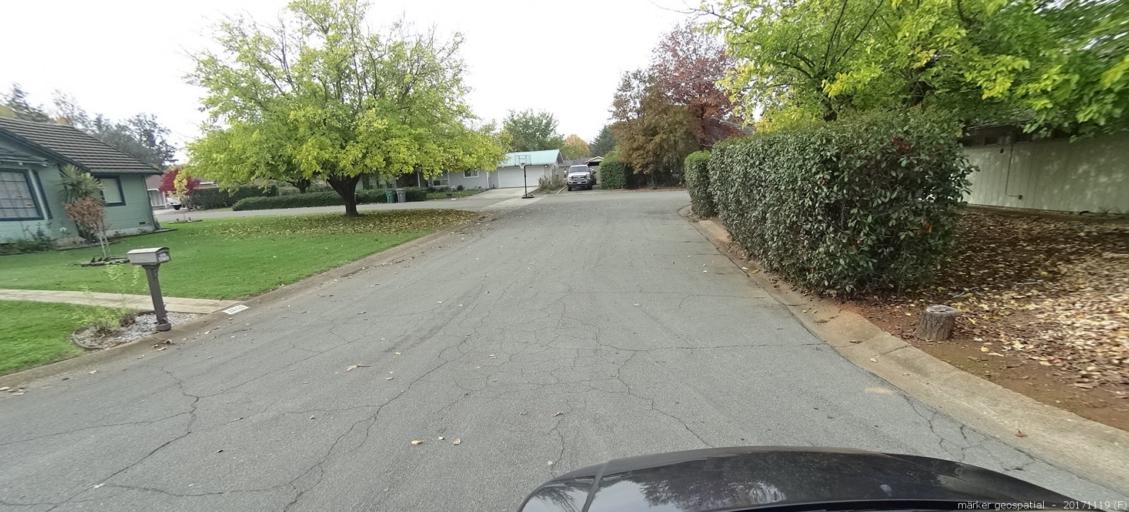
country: US
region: California
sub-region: Shasta County
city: Anderson
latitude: 40.4944
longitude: -122.3067
